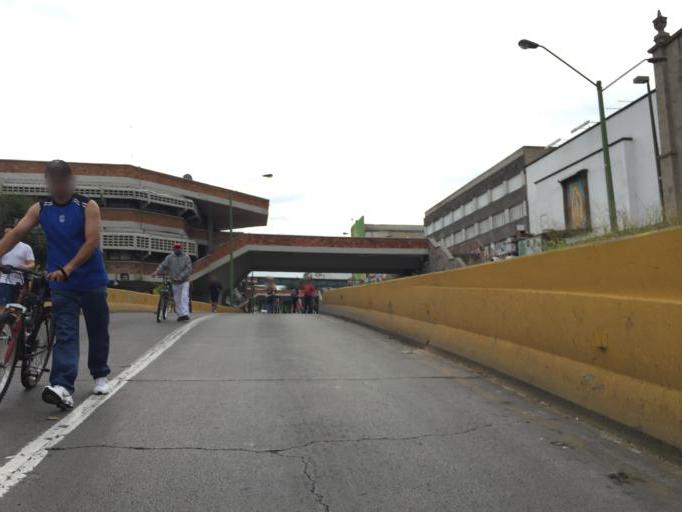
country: MX
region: Jalisco
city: Guadalajara
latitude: 20.6753
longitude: -103.3411
